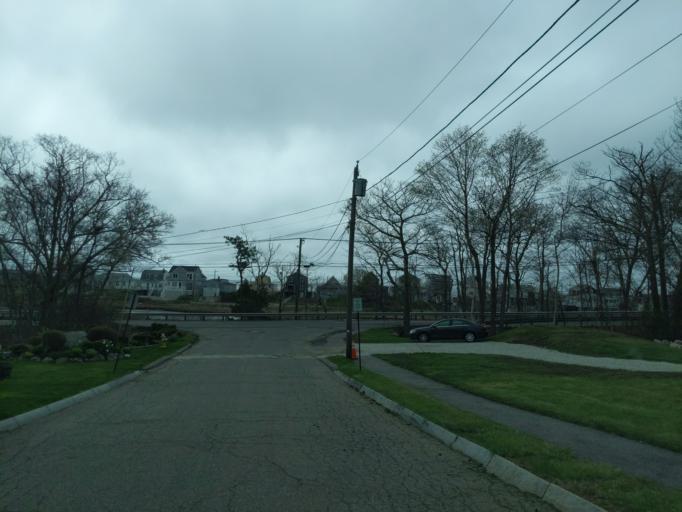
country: US
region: Massachusetts
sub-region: Essex County
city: Rockport
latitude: 42.6339
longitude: -70.6152
